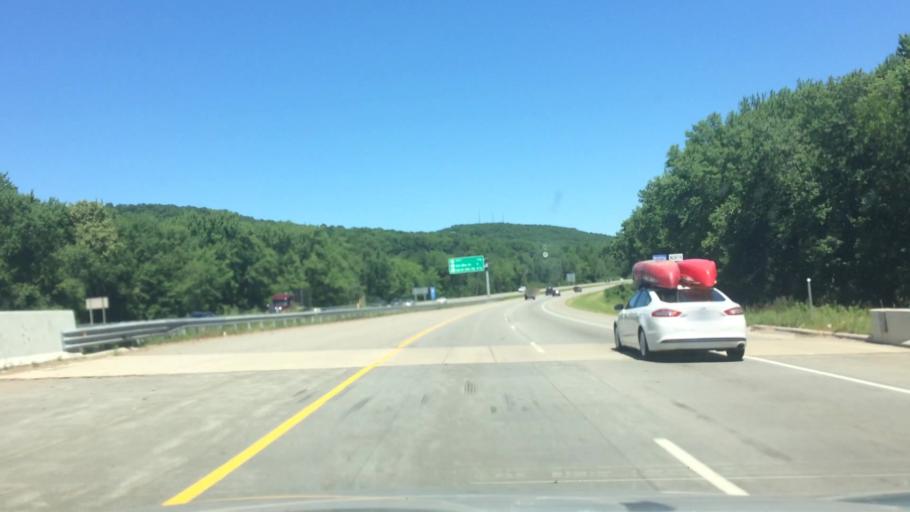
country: US
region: Wisconsin
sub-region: Marathon County
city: Evergreen
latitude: 44.8683
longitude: -89.6449
